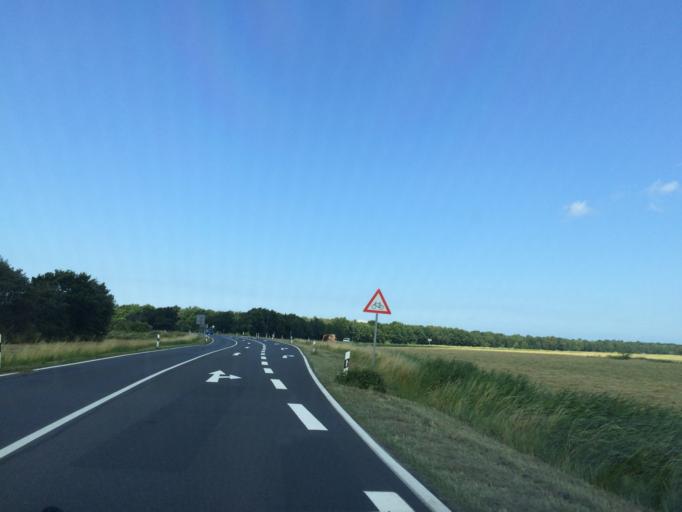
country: DE
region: Mecklenburg-Vorpommern
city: Zingst
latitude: 54.4158
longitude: 12.6612
